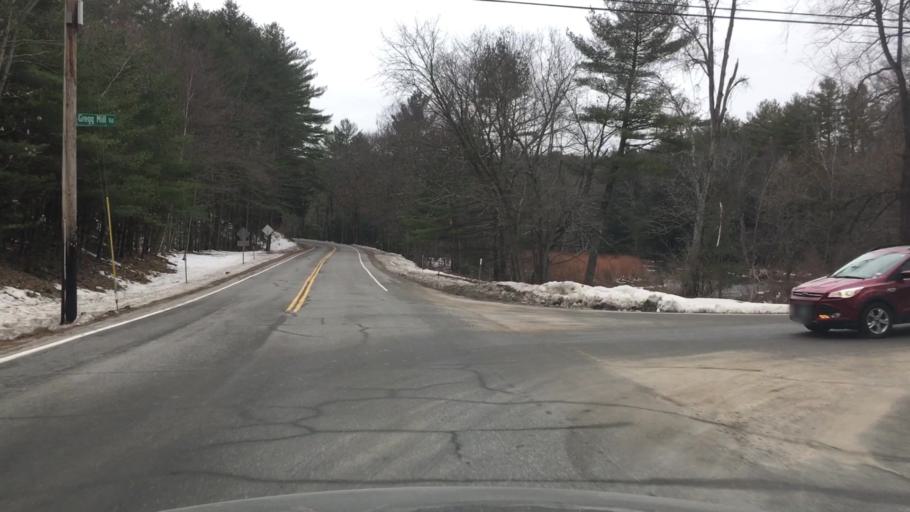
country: US
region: New Hampshire
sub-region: Hillsborough County
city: New Boston
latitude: 43.0011
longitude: -71.6621
